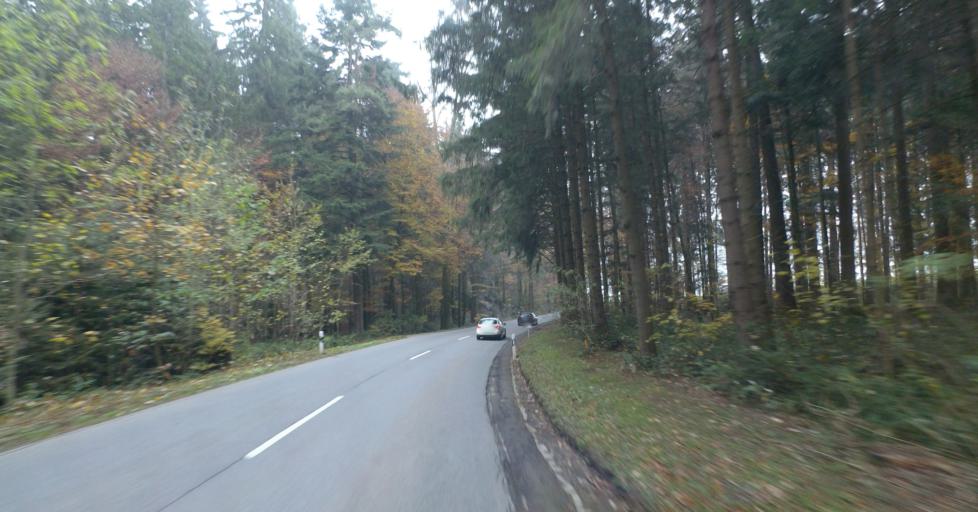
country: DE
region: Bavaria
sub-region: Upper Bavaria
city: Seeon-Seebruck
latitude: 47.9705
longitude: 12.5227
